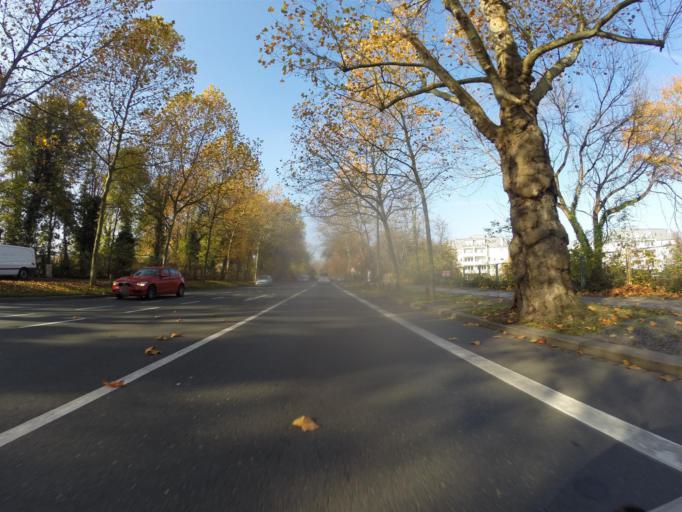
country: DE
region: Saxony
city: Leipzig
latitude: 51.3262
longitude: 12.3656
